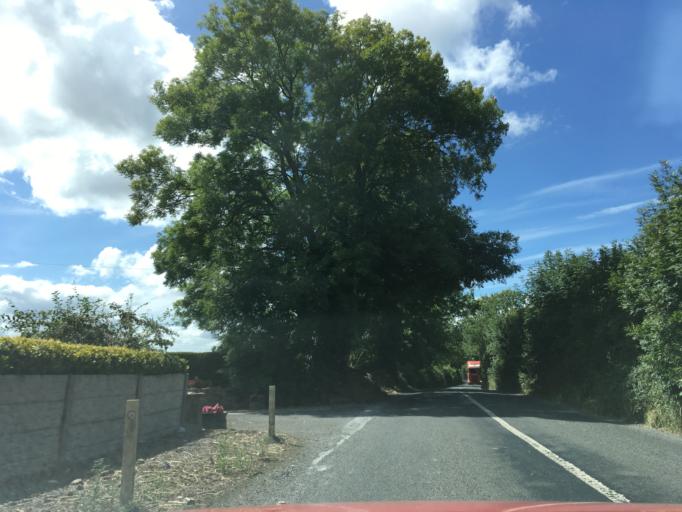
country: IE
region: Munster
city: Cahir
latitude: 52.3432
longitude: -7.9489
